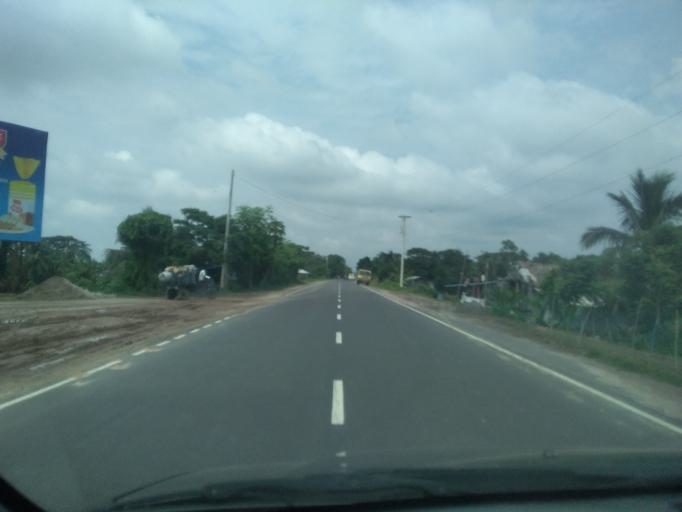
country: BD
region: Khulna
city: Kesabpur
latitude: 22.7907
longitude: 89.2196
